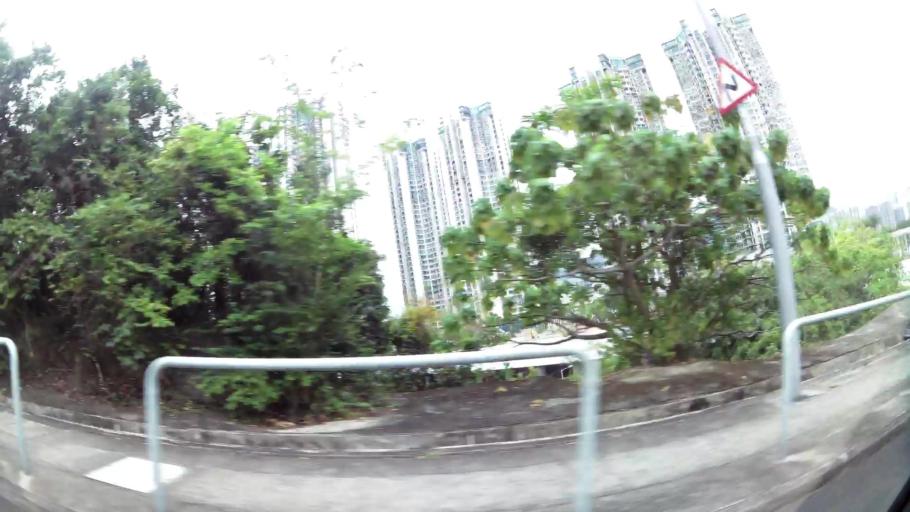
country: HK
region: Sha Tin
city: Sha Tin
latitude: 22.4002
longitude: 114.2005
